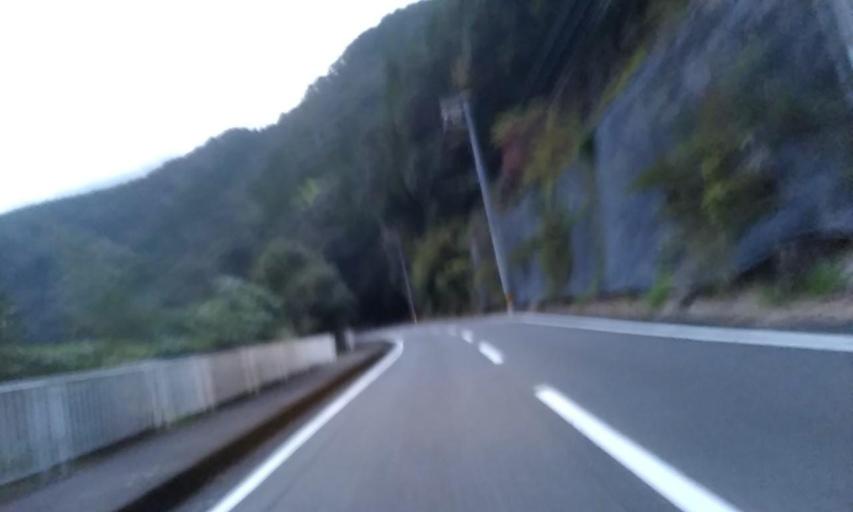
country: JP
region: Wakayama
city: Shingu
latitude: 33.7372
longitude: 135.9346
